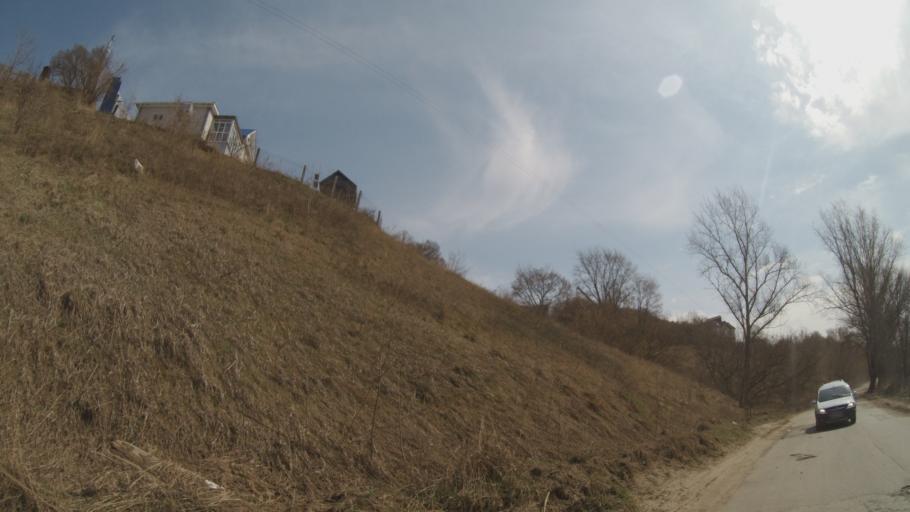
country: RU
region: Nizjnij Novgorod
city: Vyyezdnoye
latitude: 55.3915
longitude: 43.8078
